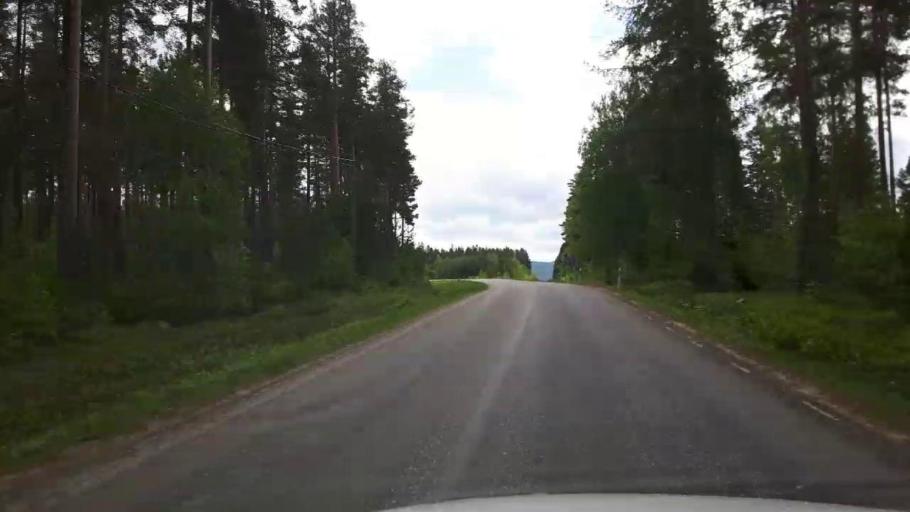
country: SE
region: Gaevleborg
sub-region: Ovanakers Kommun
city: Alfta
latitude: 61.3250
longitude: 15.9734
